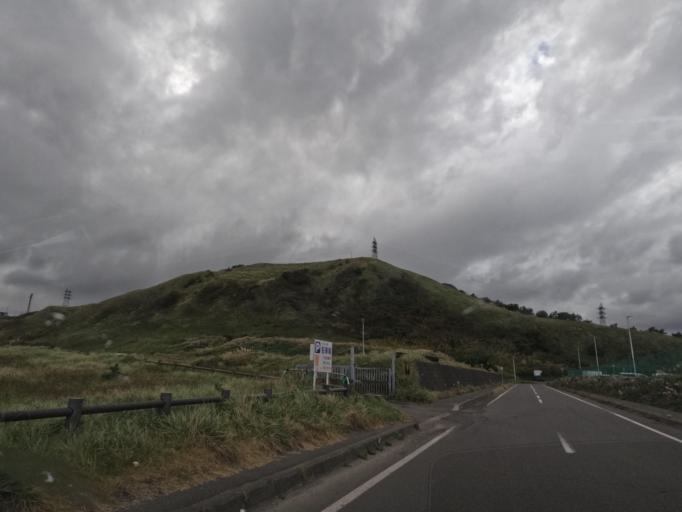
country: JP
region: Hokkaido
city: Muroran
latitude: 42.3326
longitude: 141.0225
